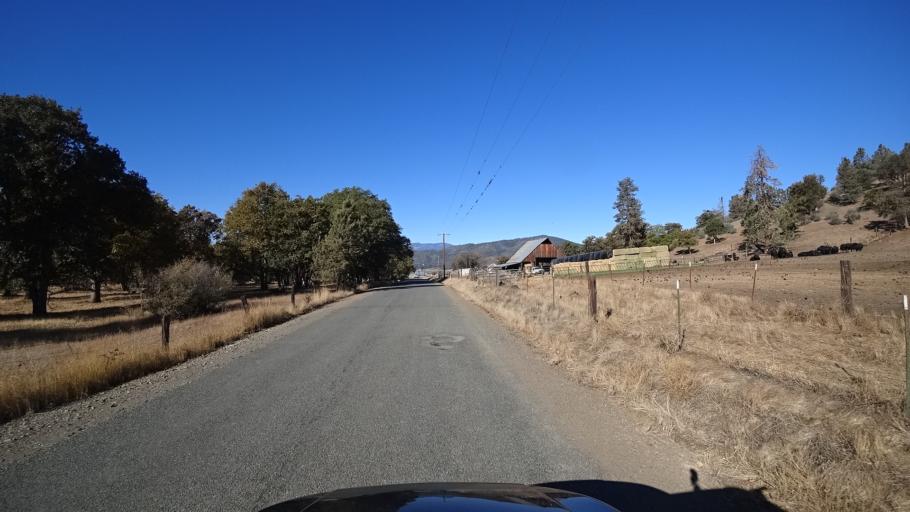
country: US
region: California
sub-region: Siskiyou County
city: Yreka
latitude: 41.5775
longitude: -122.8211
